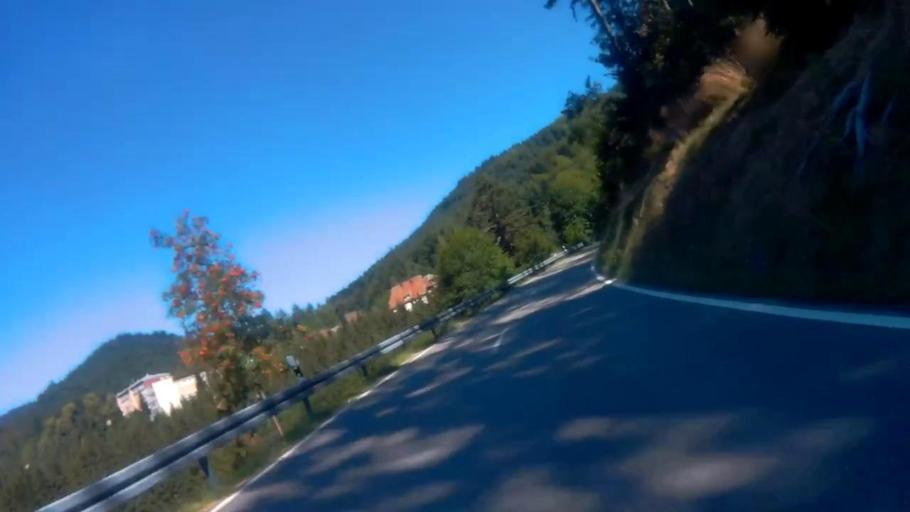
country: DE
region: Baden-Wuerttemberg
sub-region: Freiburg Region
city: Badenweiler
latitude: 47.7791
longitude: 7.7362
